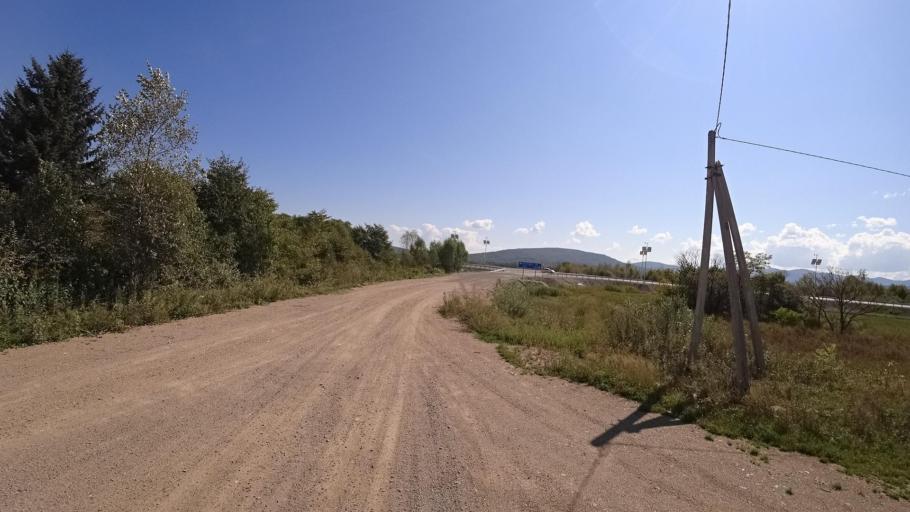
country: RU
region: Jewish Autonomous Oblast
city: Londoko
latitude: 49.0033
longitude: 131.9447
